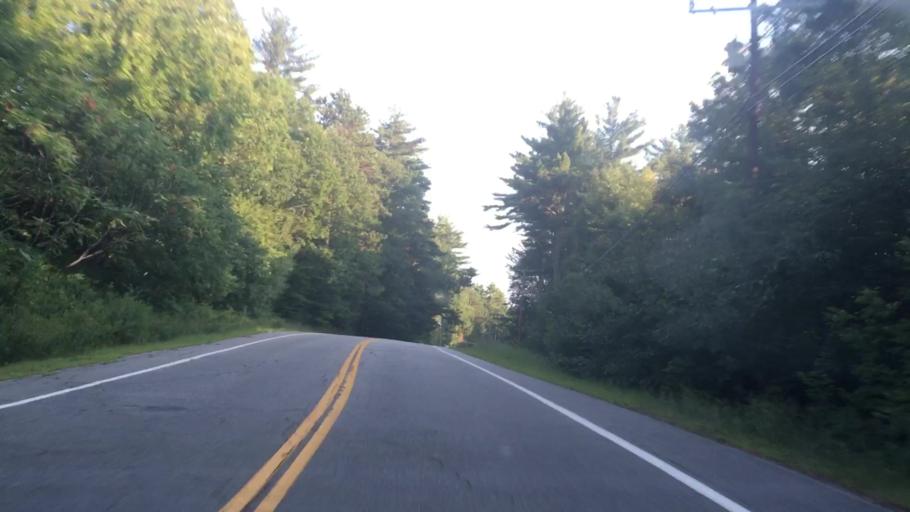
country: US
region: New Hampshire
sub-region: Belknap County
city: Gilmanton
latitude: 43.4552
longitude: -71.4216
